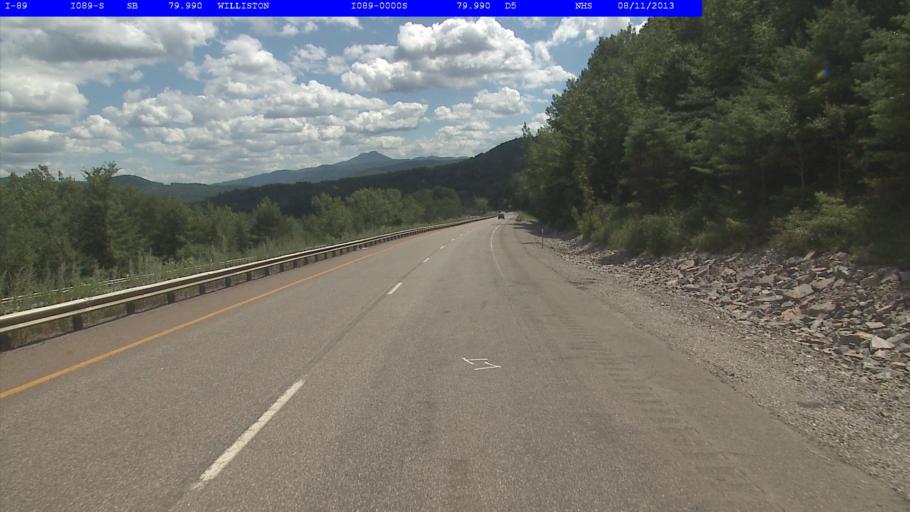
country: US
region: Vermont
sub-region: Chittenden County
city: Williston
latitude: 44.4296
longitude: -73.0372
